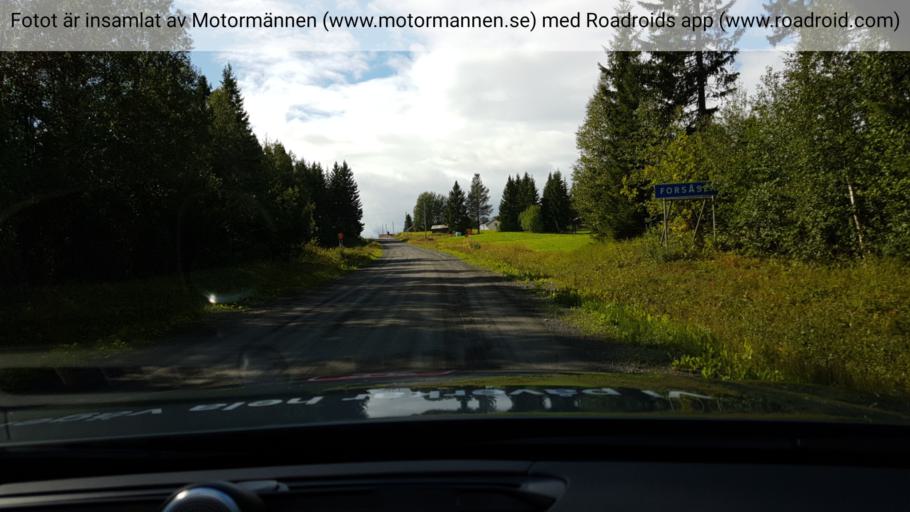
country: SE
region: Jaemtland
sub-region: OEstersunds Kommun
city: Lit
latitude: 63.6775
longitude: 14.7269
